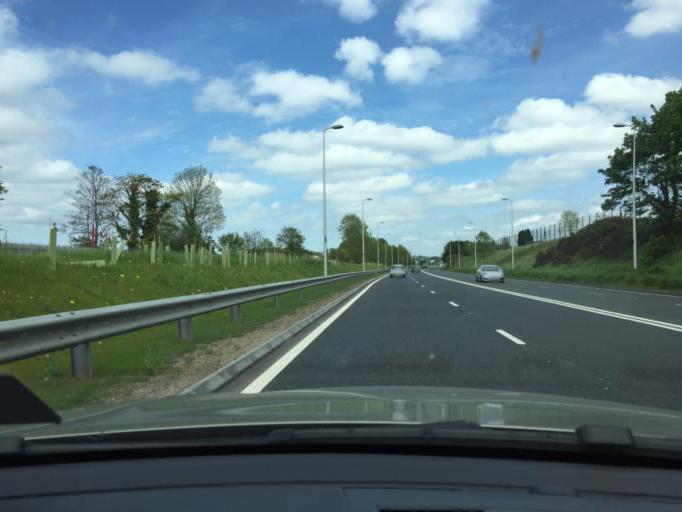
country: GB
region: Northern Ireland
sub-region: Armagh District
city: Portadown
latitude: 54.4362
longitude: -6.4279
